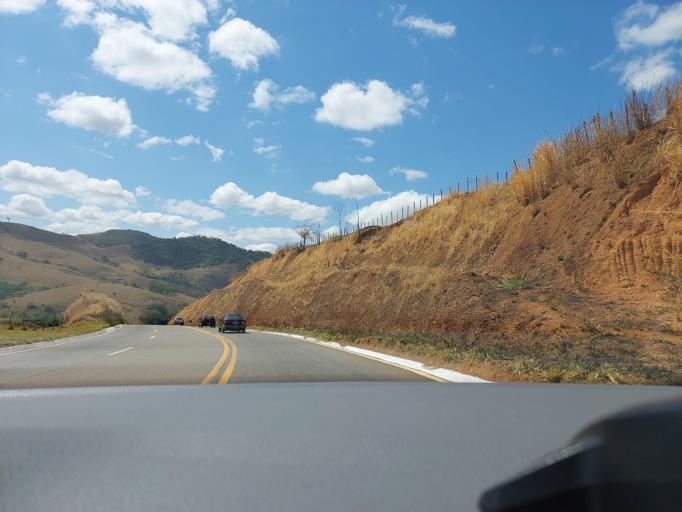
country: BR
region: Minas Gerais
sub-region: Muriae
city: Muriae
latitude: -21.0920
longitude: -42.4797
